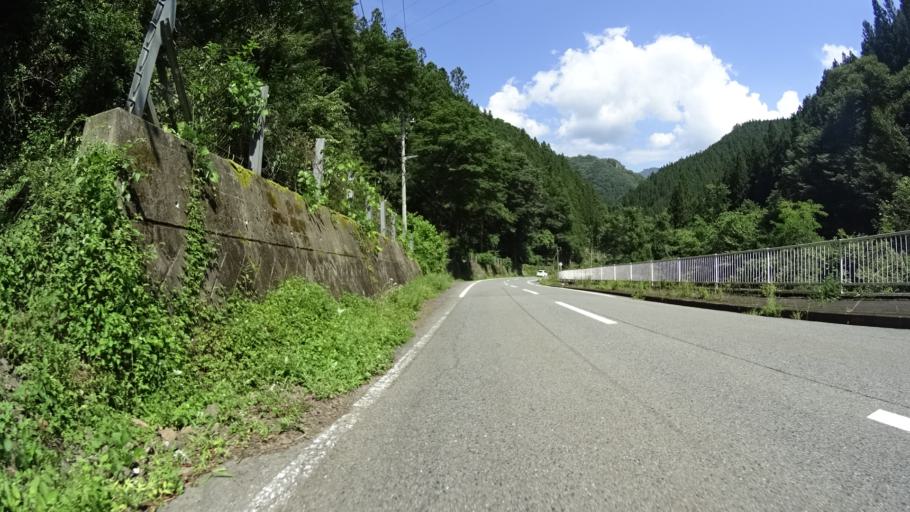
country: JP
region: Gunma
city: Tomioka
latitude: 36.0772
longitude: 138.8252
